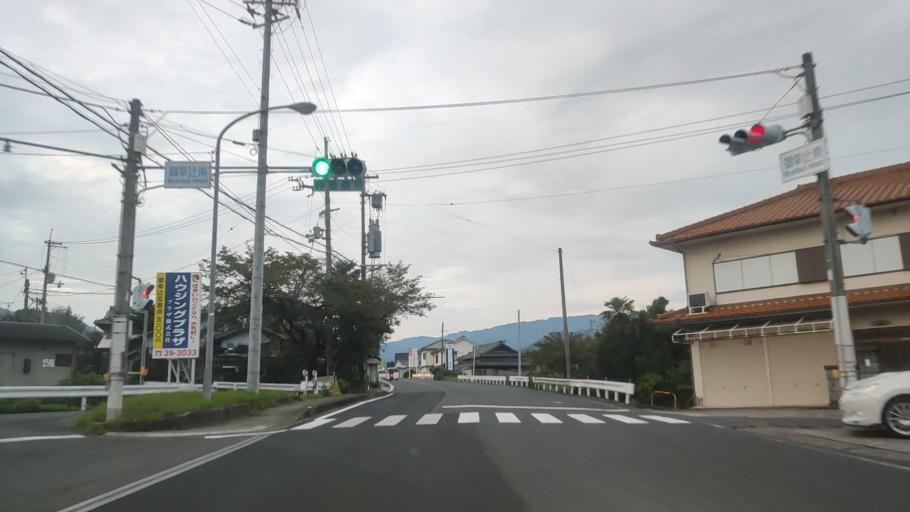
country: JP
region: Wakayama
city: Hashimoto
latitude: 34.3343
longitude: 135.6058
